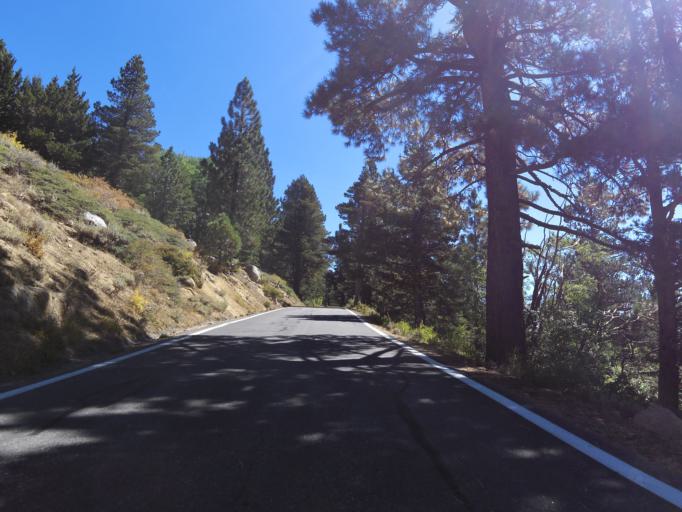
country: US
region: Nevada
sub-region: Douglas County
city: Gardnerville Ranchos
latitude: 38.5476
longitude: -119.8349
